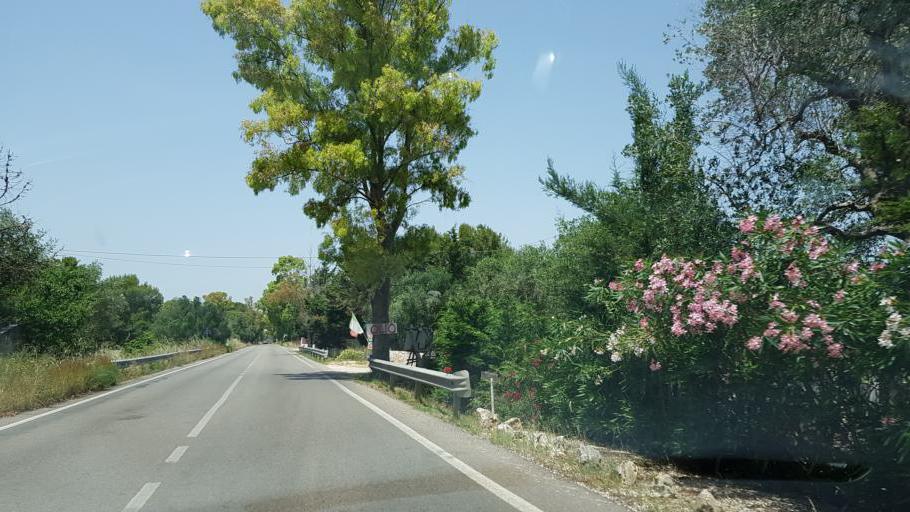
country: IT
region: Apulia
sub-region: Provincia di Lecce
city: Porto Cesareo
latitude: 40.2590
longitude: 17.9236
